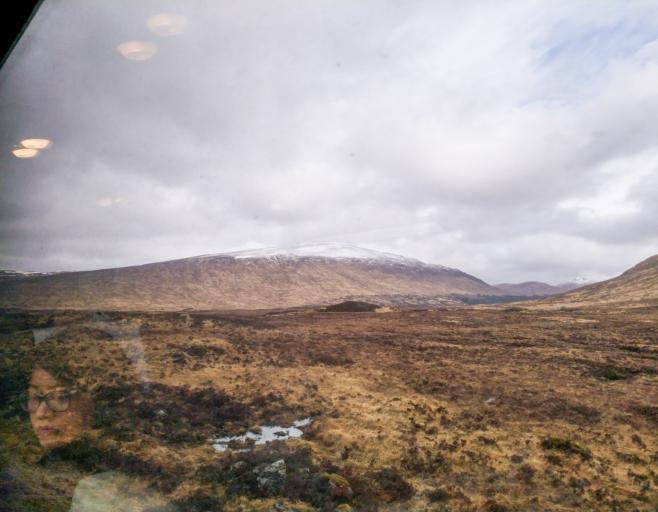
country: GB
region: Scotland
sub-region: Highland
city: Spean Bridge
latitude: 56.7498
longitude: -4.6755
